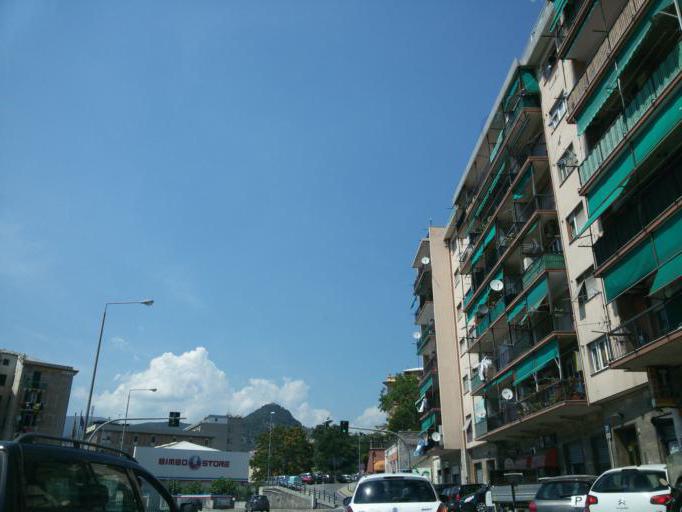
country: IT
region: Liguria
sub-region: Provincia di Genova
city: San Teodoro
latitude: 44.4195
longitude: 8.8592
